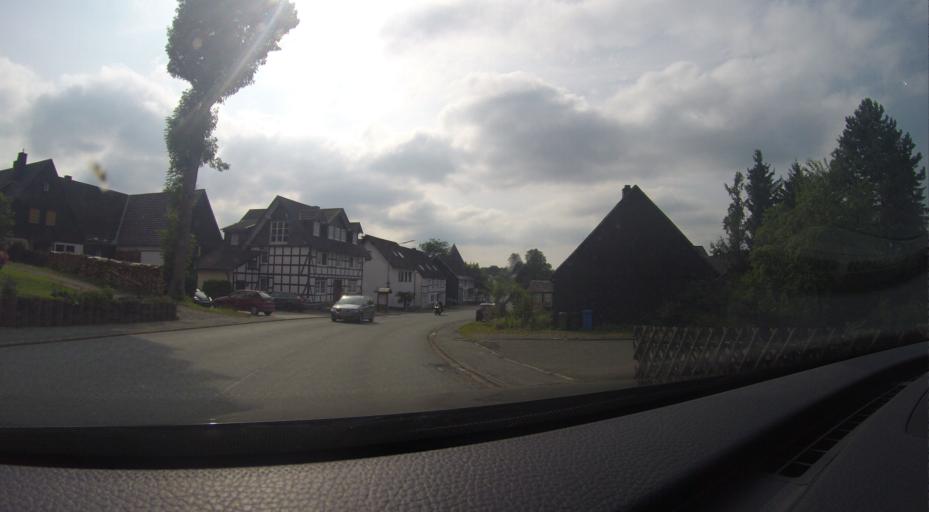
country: DE
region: Hesse
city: Willingen
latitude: 51.2228
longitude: 8.6071
